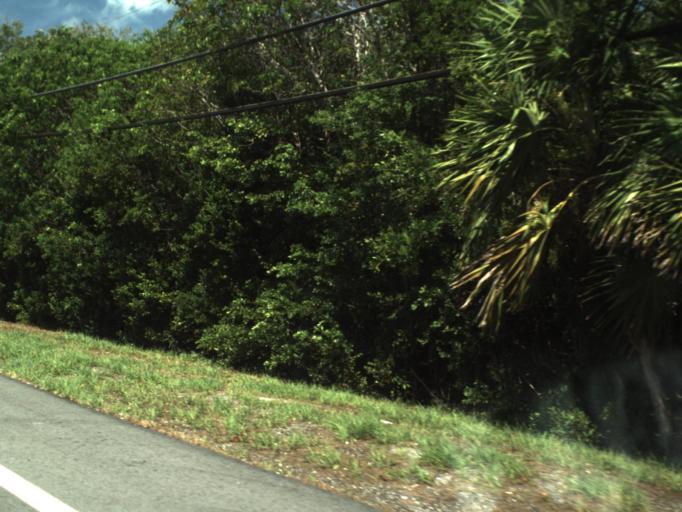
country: US
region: Florida
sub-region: Monroe County
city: Marathon
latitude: 24.7448
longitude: -80.9875
